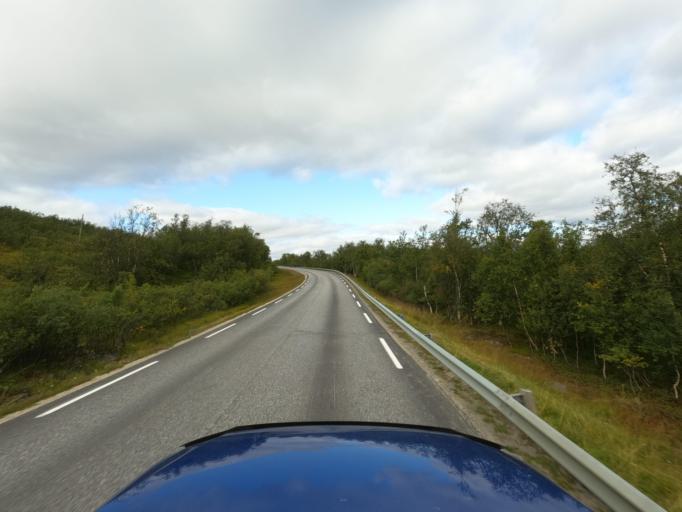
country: NO
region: Finnmark Fylke
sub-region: Porsanger
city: Lakselv
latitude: 70.1516
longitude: 24.8979
